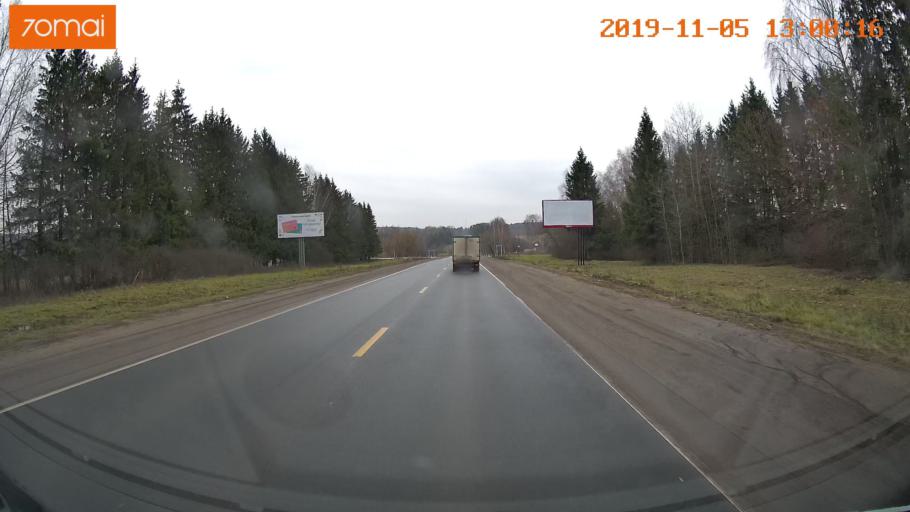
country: RU
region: Ivanovo
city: Kokhma
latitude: 56.9147
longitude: 41.1424
